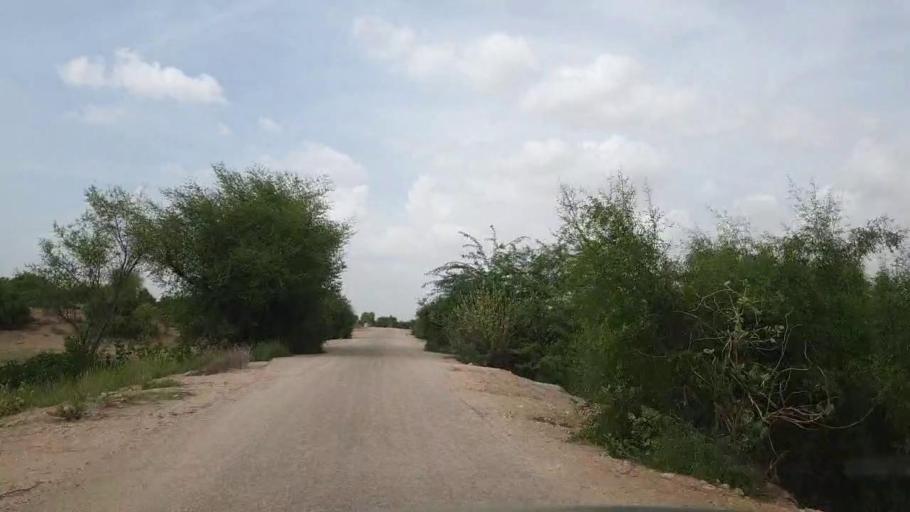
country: PK
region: Sindh
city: Kot Diji
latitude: 27.2107
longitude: 69.0829
